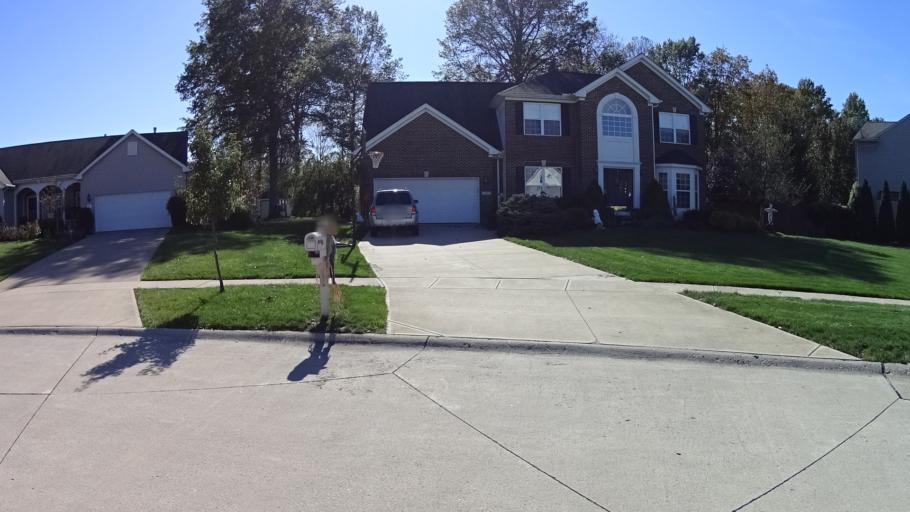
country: US
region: Ohio
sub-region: Lorain County
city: Amherst
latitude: 41.3868
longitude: -82.2379
